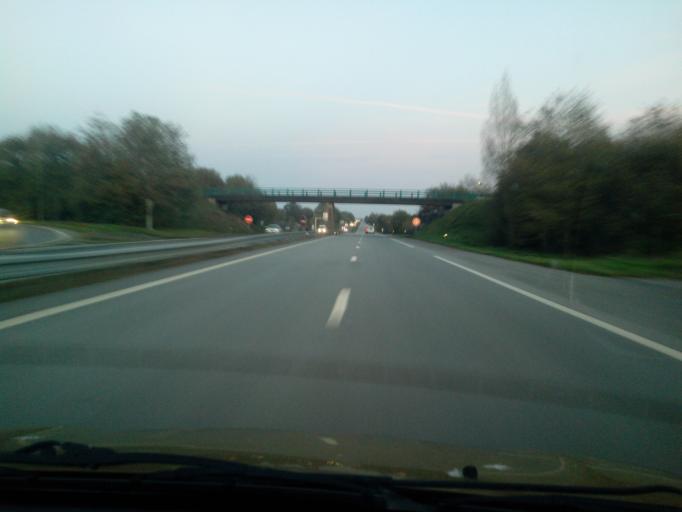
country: FR
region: Brittany
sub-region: Departement du Morbihan
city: Reguiny
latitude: 47.9198
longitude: -2.7218
